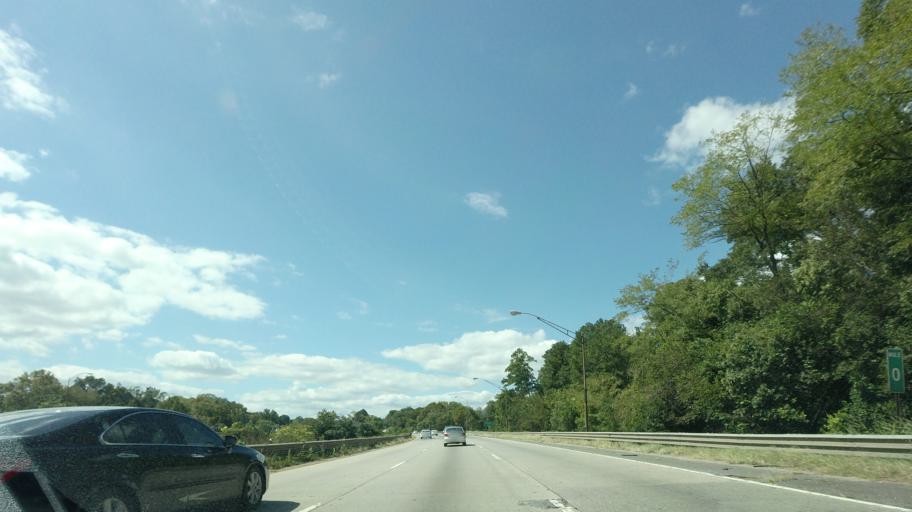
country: US
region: Georgia
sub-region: Bibb County
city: Macon
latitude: 32.8534
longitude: -83.6331
